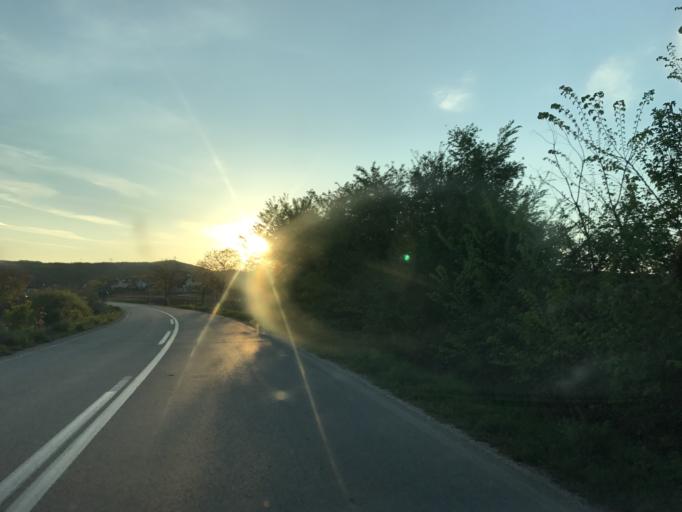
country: RO
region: Mehedinti
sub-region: Comuna Burila Mare
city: Burila Mare
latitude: 44.4878
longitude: 22.4640
